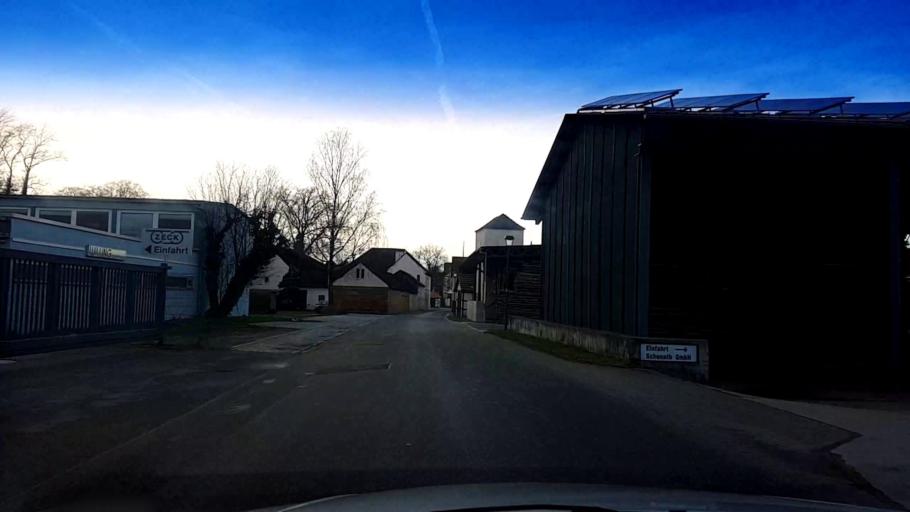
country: DE
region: Bavaria
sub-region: Upper Franconia
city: Schesslitz
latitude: 49.9881
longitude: 11.0477
